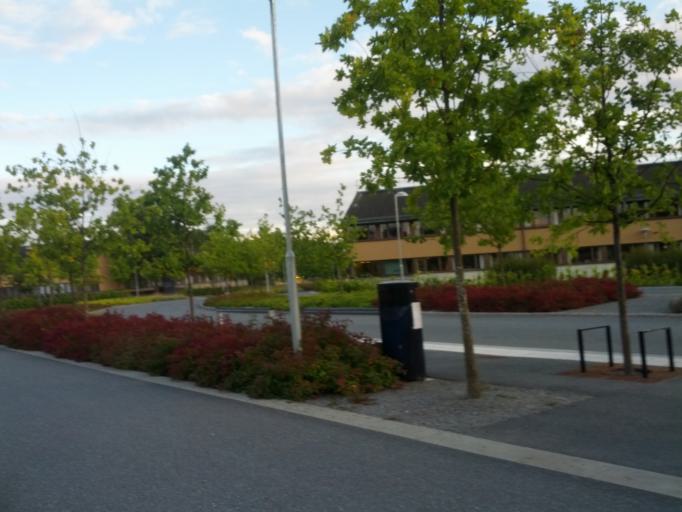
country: SE
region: Uppsala
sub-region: Uppsala Kommun
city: Saevja
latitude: 59.8186
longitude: 17.6586
